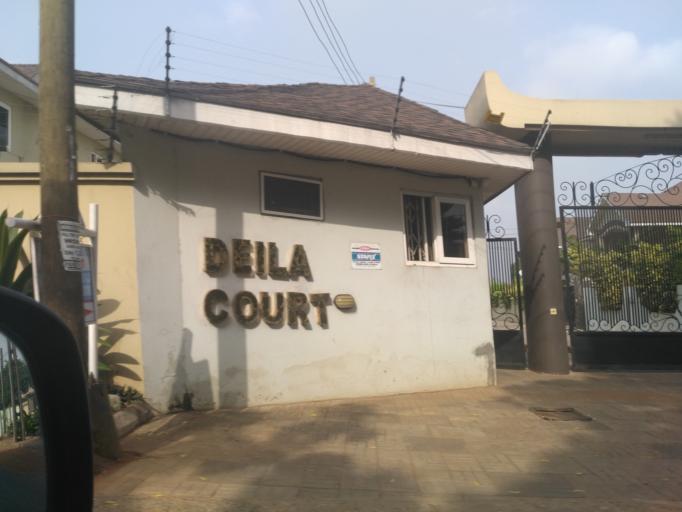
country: GH
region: Greater Accra
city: Accra
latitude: 5.6049
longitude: -0.1868
